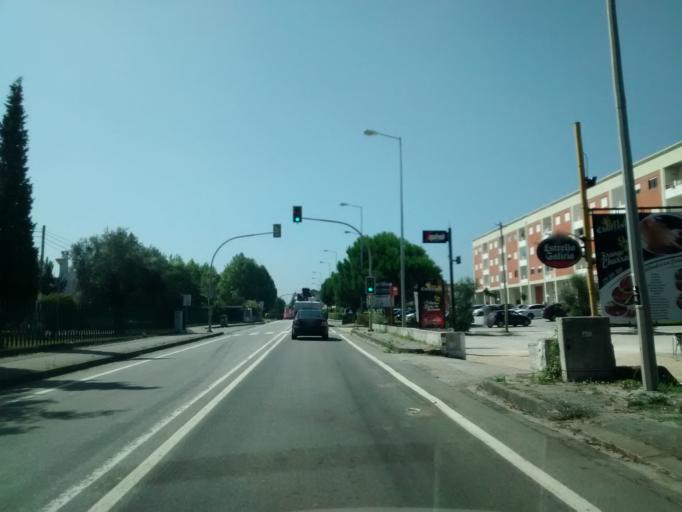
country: PT
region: Aveiro
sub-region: Mealhada
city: Mealhada
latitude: 40.3875
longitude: -8.4506
